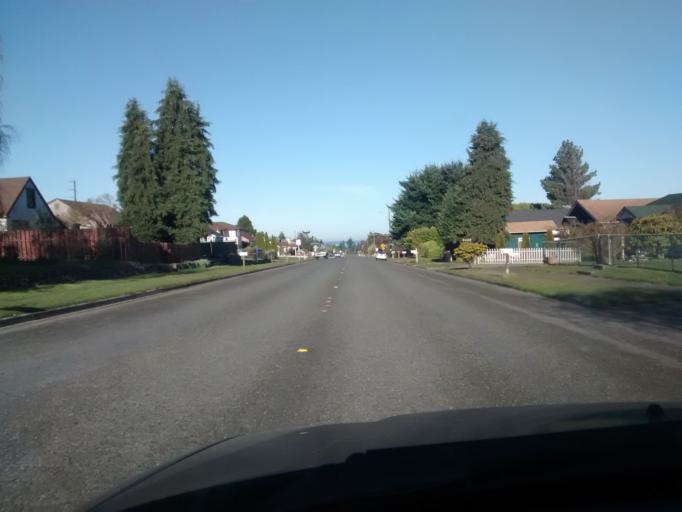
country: US
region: Washington
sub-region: Clallam County
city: Port Angeles
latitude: 48.1271
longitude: -123.4652
